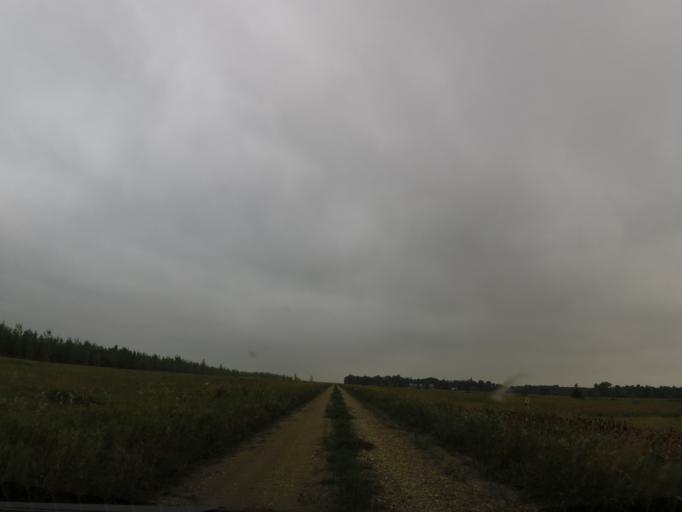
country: US
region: North Dakota
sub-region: Walsh County
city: Grafton
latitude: 48.4246
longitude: -97.1181
